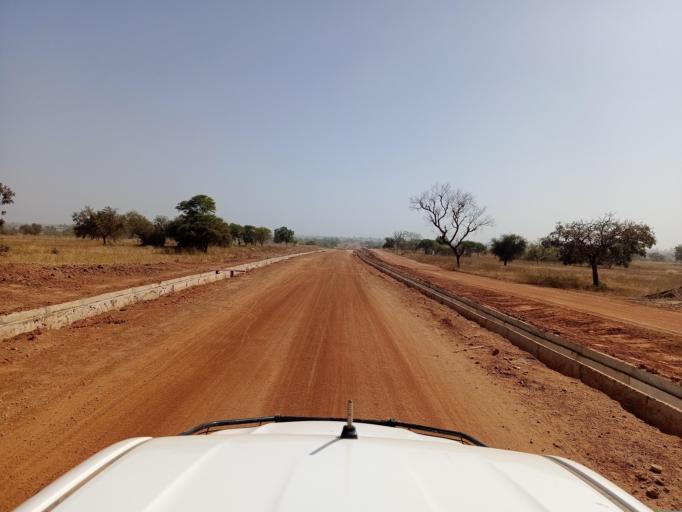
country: BF
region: Centre-Est
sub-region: Province du Boulgou
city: Garango
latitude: 11.5011
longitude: -0.5079
